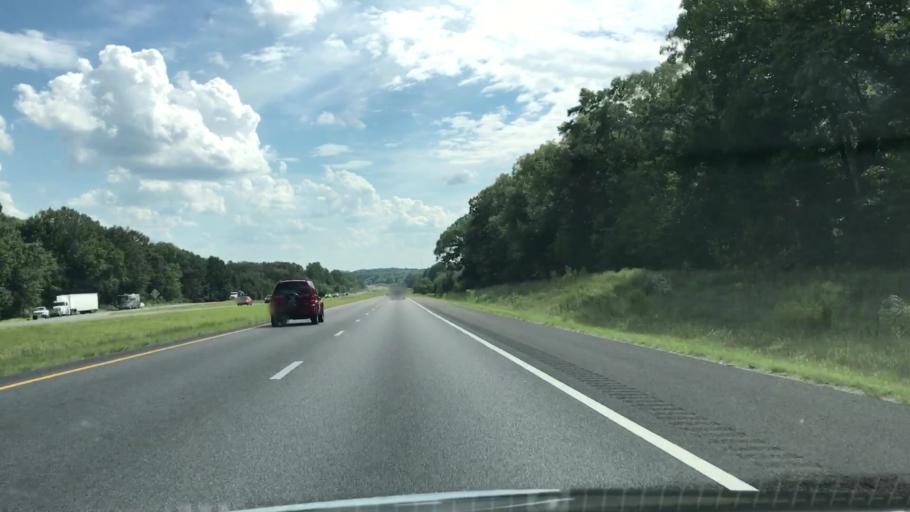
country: US
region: Tennessee
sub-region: Maury County
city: Spring Hill
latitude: 35.6813
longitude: -86.8882
